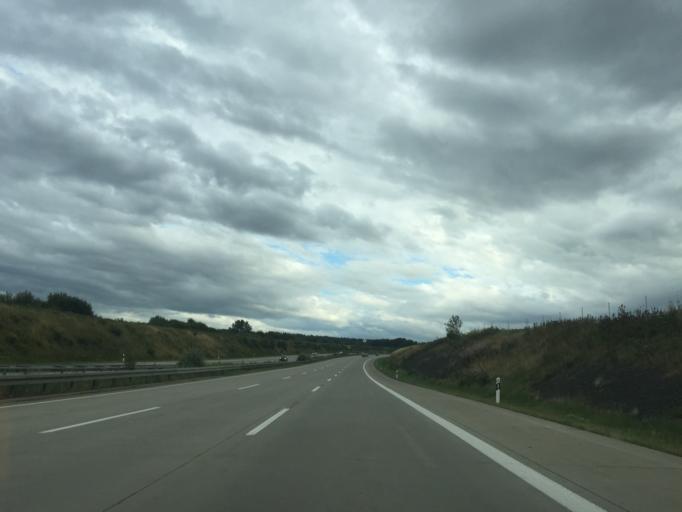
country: DE
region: Thuringia
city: Tanna
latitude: 50.4756
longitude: 11.8023
